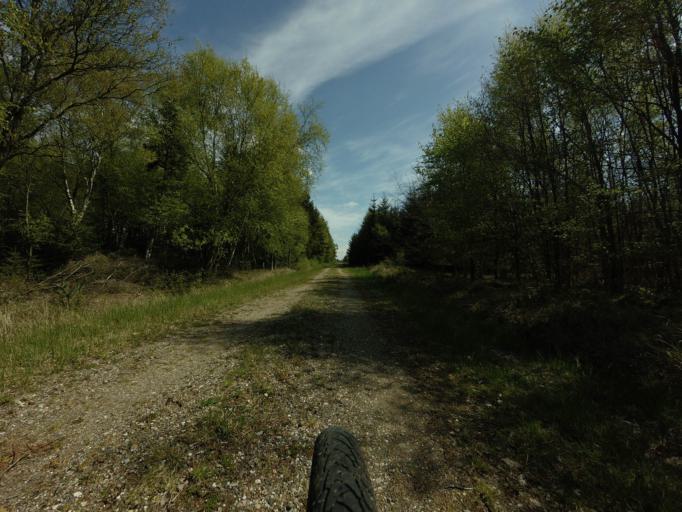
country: DK
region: North Denmark
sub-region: Jammerbugt Kommune
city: Brovst
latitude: 57.1692
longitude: 9.5493
